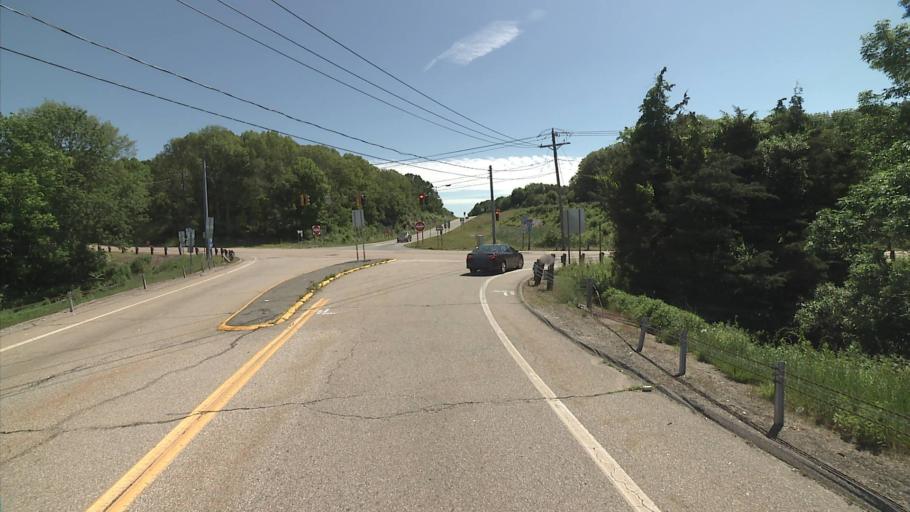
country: US
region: Connecticut
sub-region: New London County
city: Pawcatuck
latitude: 41.4209
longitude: -71.8451
